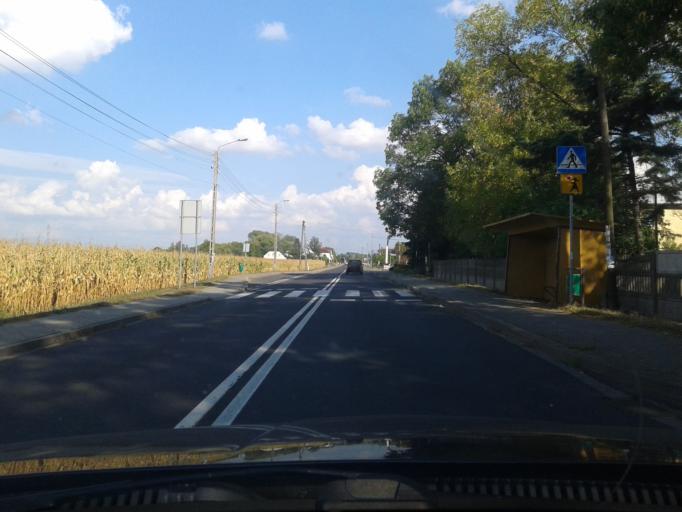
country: PL
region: Silesian Voivodeship
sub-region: Powiat wodzislawski
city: Olza
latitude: 49.9545
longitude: 18.3462
